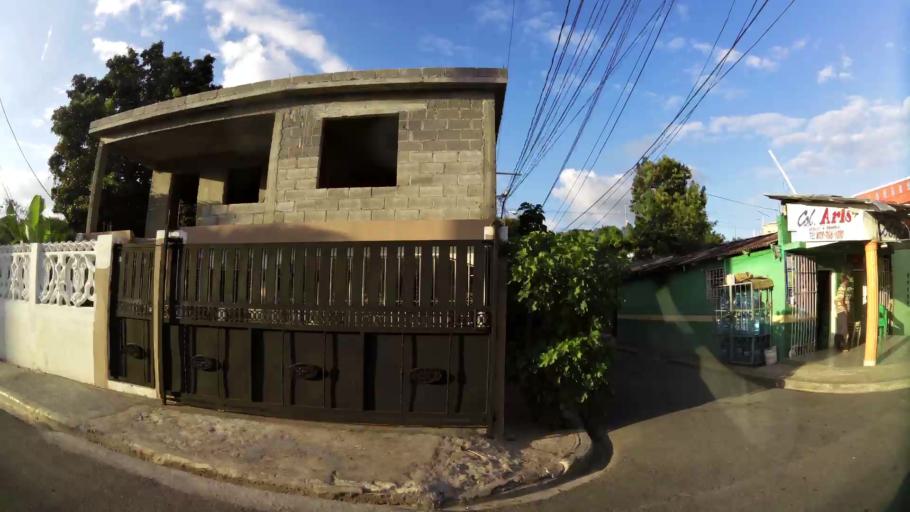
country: DO
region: Santo Domingo
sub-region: Santo Domingo
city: Santo Domingo Este
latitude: 18.4830
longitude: -69.8376
